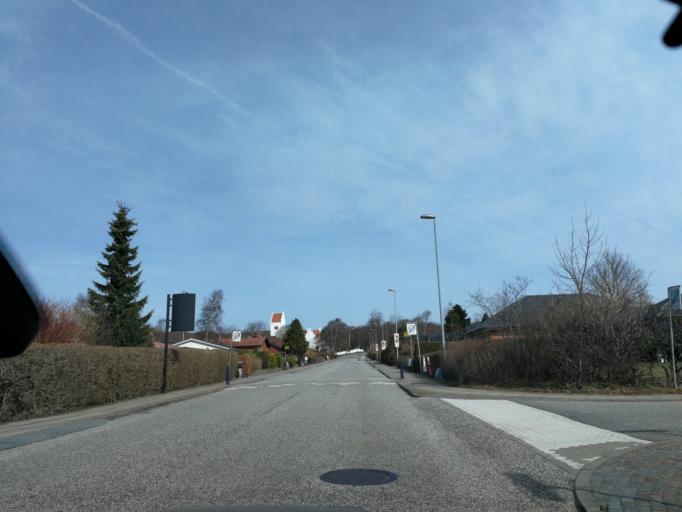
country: DK
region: North Denmark
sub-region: Alborg Kommune
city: Vodskov
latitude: 57.1089
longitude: 10.0265
